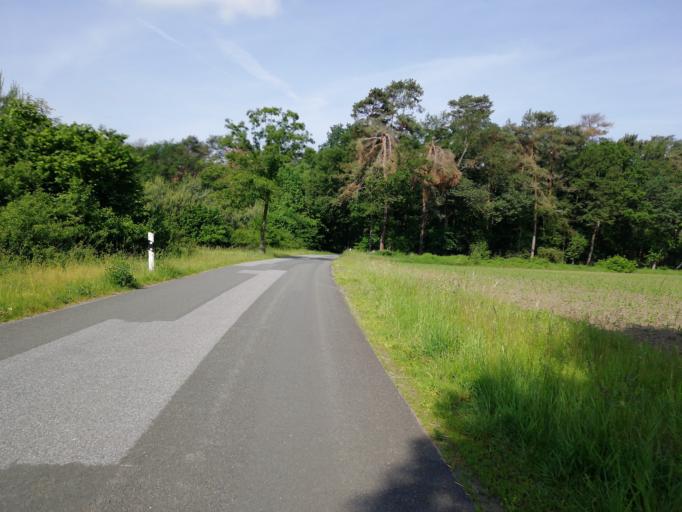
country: DE
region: North Rhine-Westphalia
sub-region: Regierungsbezirk Detmold
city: Verl
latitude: 51.9034
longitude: 8.5044
